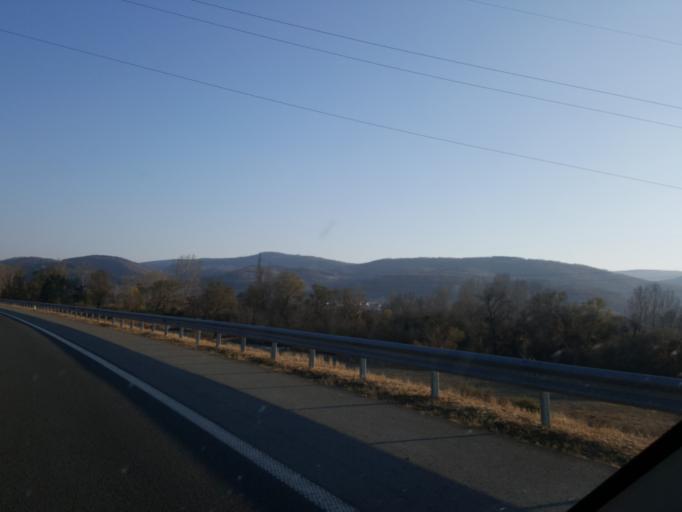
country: RS
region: Central Serbia
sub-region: Pirotski Okrug
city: Dimitrovgrad
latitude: 43.0252
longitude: 22.7252
